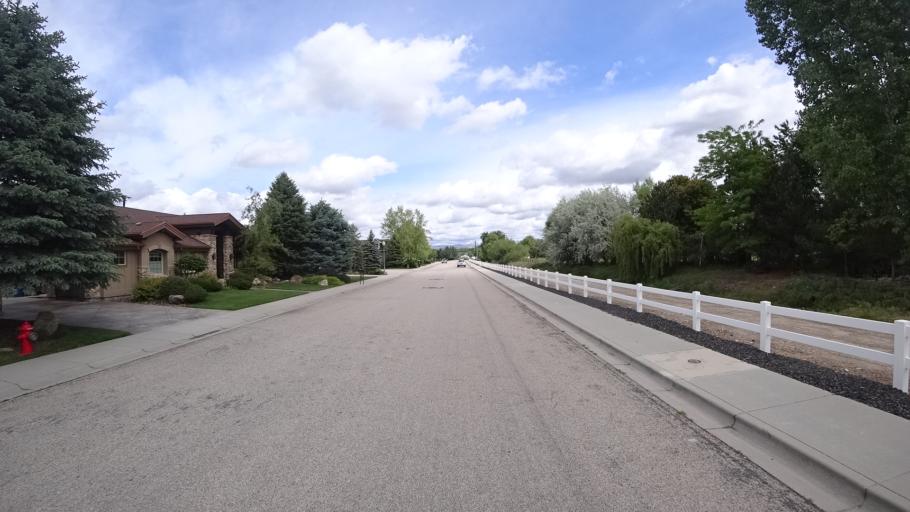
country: US
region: Idaho
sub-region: Ada County
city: Eagle
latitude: 43.6748
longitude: -116.3043
